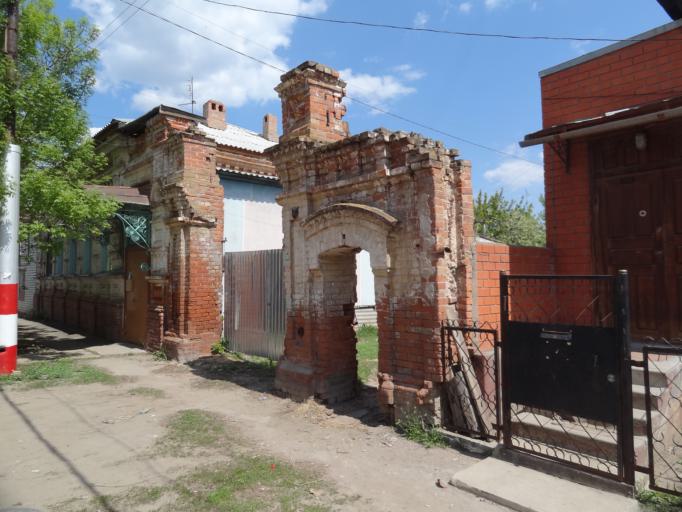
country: RU
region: Saratov
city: Engel's
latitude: 51.4999
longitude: 46.1318
